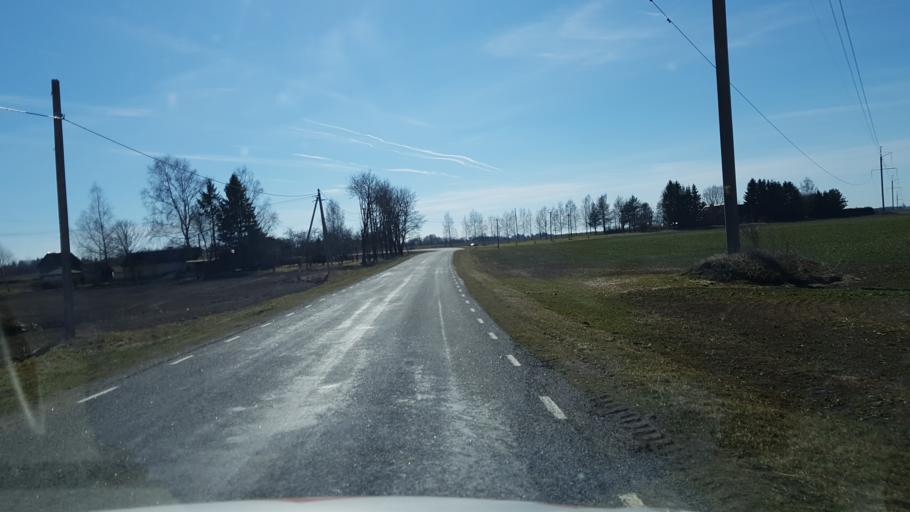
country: EE
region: Laeaene-Virumaa
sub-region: Someru vald
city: Someru
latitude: 59.3243
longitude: 26.5043
